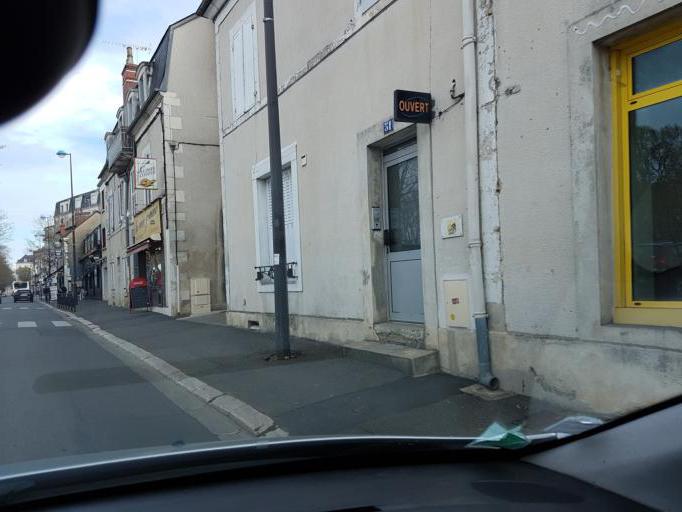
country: FR
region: Centre
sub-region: Departement du Cher
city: Bourges
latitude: 47.0764
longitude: 2.4010
